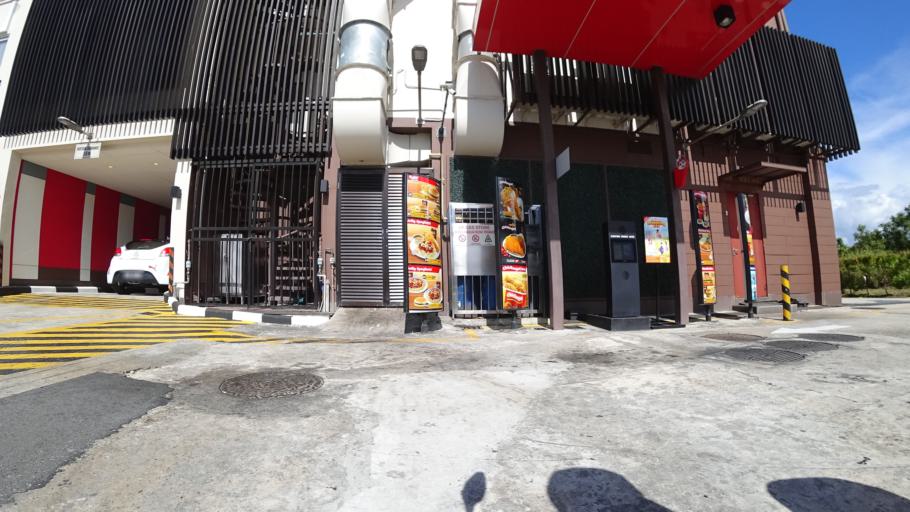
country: BN
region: Brunei and Muara
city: Bandar Seri Begawan
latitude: 4.8685
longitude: 114.8624
